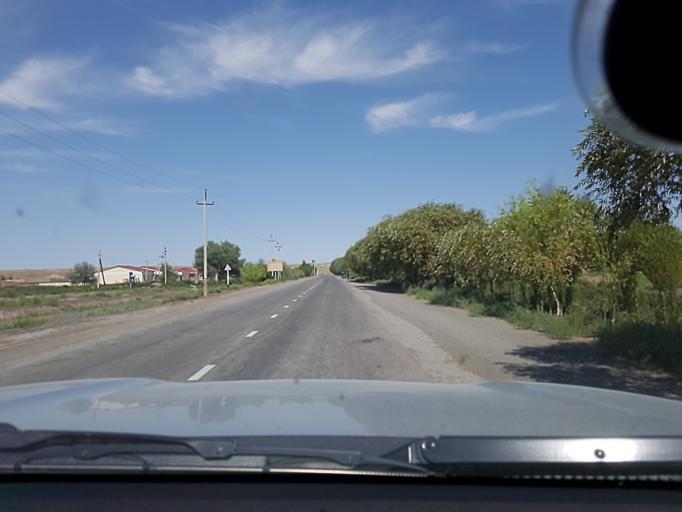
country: UZ
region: Karakalpakstan
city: Mang'it Shahri
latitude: 42.2405
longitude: 60.1461
